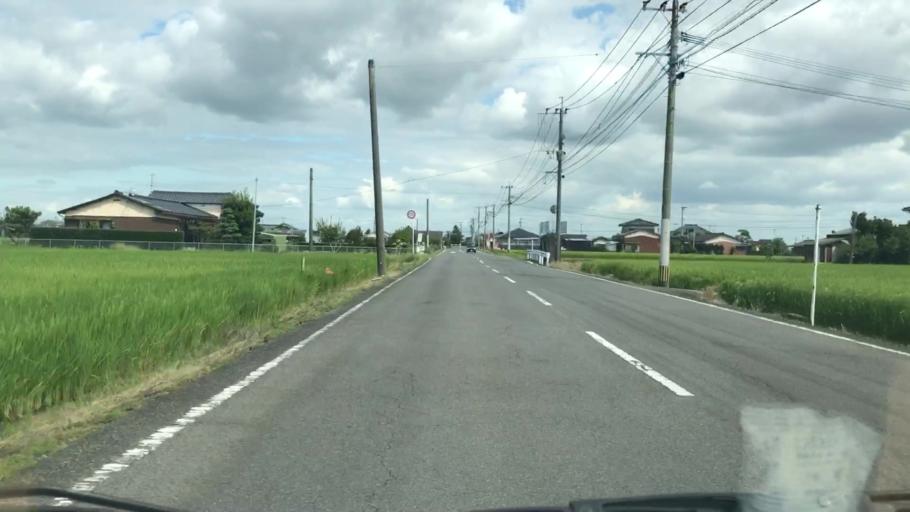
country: JP
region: Saga Prefecture
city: Saga-shi
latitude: 33.1956
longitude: 130.1884
